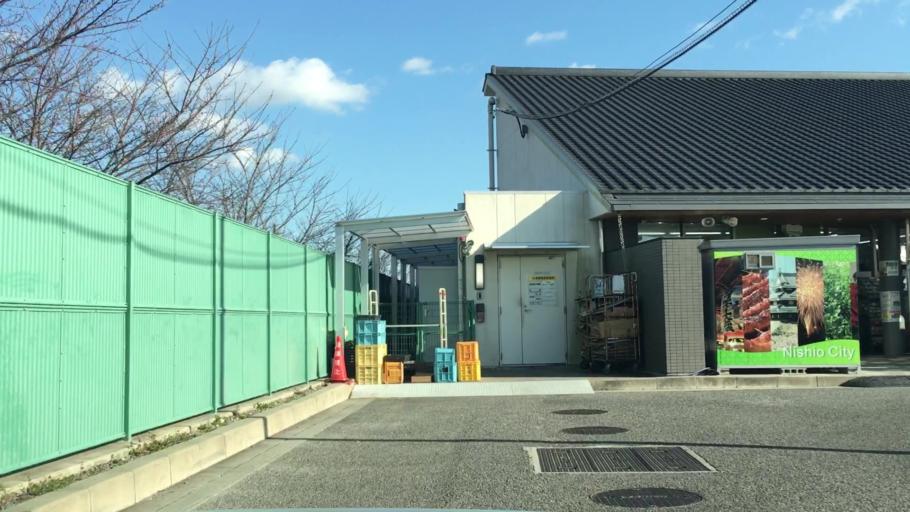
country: JP
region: Aichi
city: Nishio
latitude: 34.8770
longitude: 137.0831
